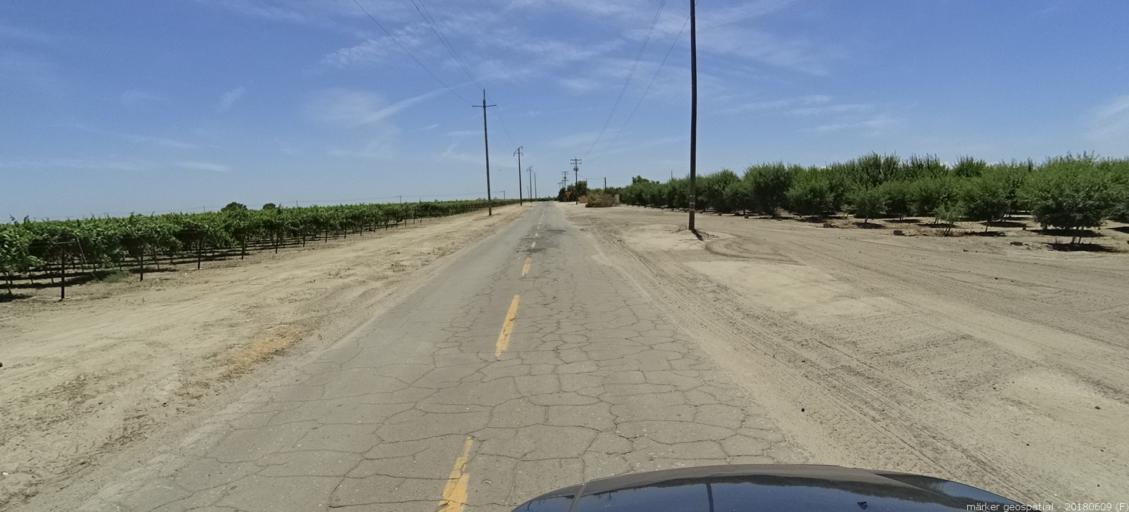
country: US
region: California
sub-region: Fresno County
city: Biola
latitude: 36.8397
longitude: -120.1102
